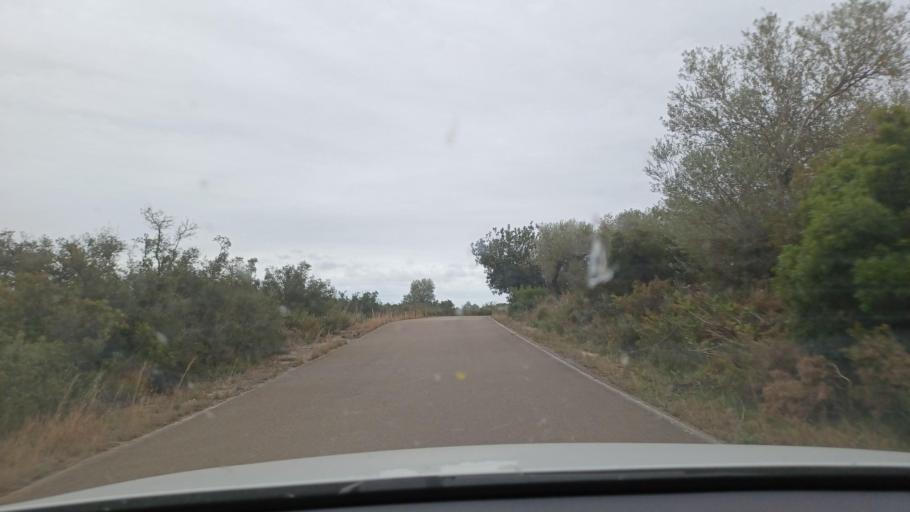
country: ES
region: Valencia
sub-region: Provincia de Castello
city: Canet lo Roig
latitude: 40.5953
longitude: 0.2829
